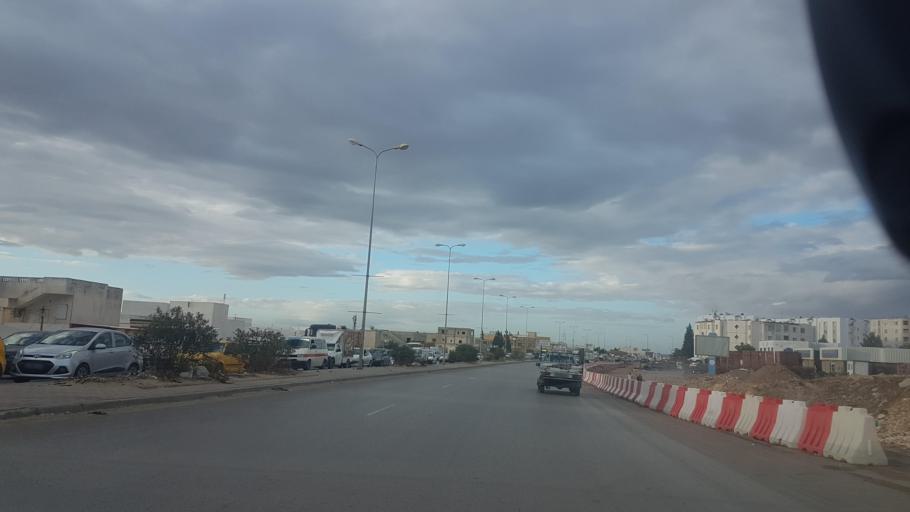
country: TN
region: Bin 'Arus
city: Ben Arous
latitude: 36.7422
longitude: 10.2072
